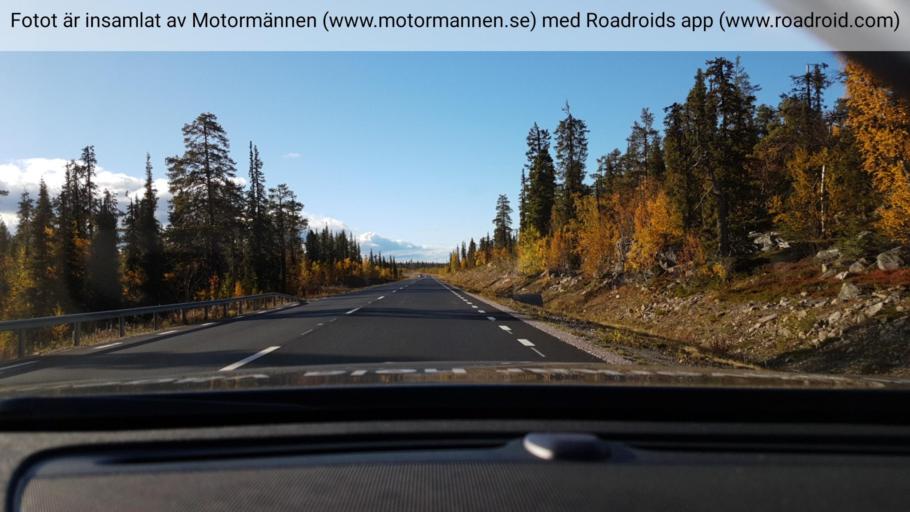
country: SE
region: Norrbotten
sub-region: Jokkmokks Kommun
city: Jokkmokk
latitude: 67.0423
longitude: 20.0689
